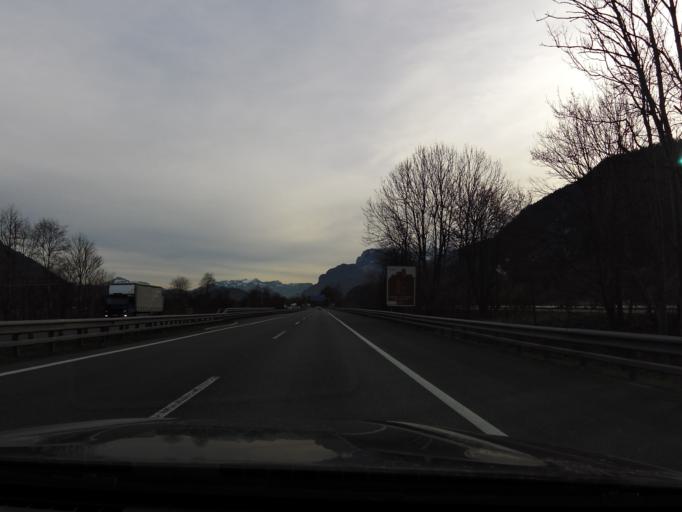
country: AT
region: Tyrol
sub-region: Politischer Bezirk Kufstein
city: Schwoich
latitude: 47.5557
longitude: 12.1278
